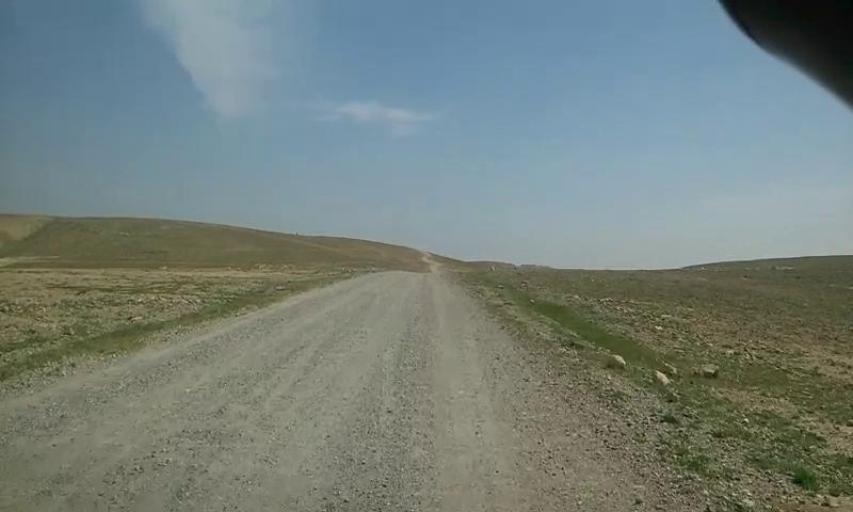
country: PS
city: `Arab ar Rashaydah
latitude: 31.5257
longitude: 35.2959
